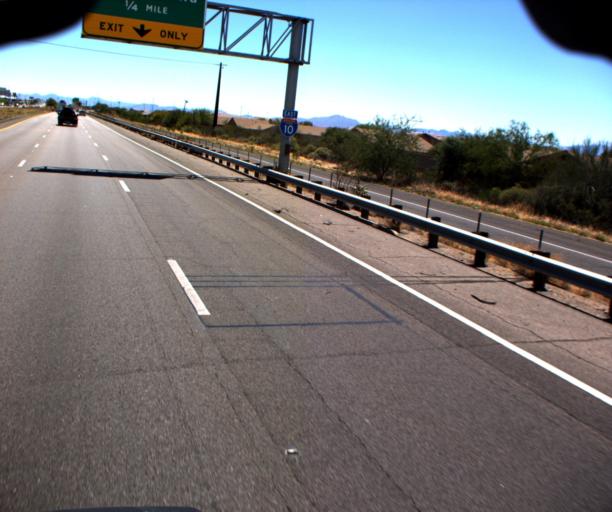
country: US
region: Arizona
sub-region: Pima County
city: Summit
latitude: 32.1309
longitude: -110.8844
